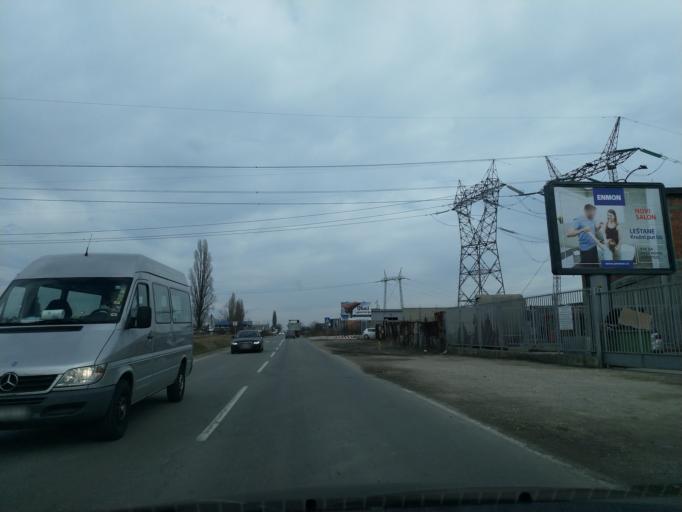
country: RS
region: Central Serbia
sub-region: Belgrade
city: Zvezdara
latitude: 44.7344
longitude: 20.5887
